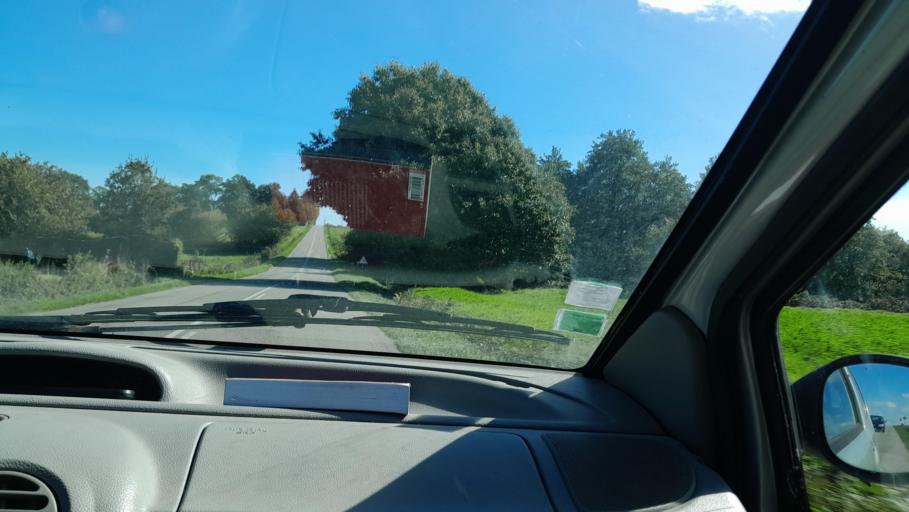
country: FR
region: Pays de la Loire
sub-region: Departement de la Mayenne
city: Cosse-le-Vivien
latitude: 47.9377
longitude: -0.8646
